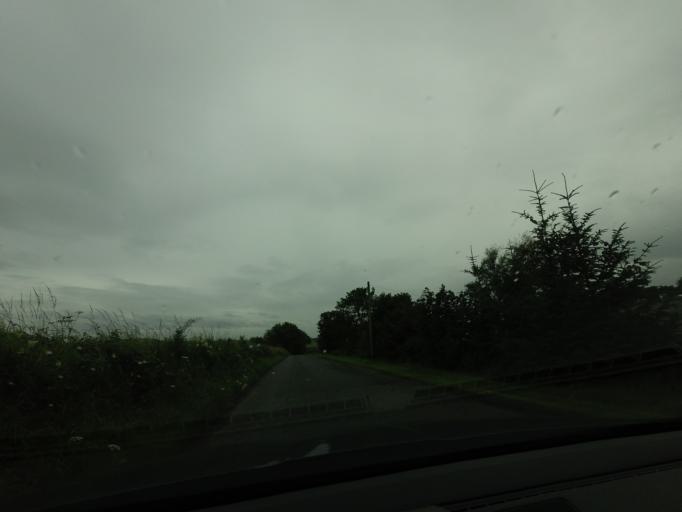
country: GB
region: Scotland
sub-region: Aberdeenshire
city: Portsoy
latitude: 57.6521
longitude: -2.6553
